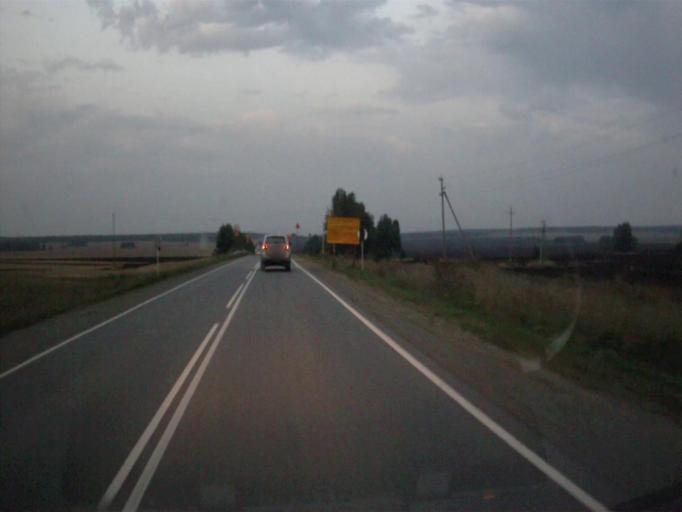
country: RU
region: Chelyabinsk
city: Timiryazevskiy
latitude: 55.2060
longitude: 60.7918
